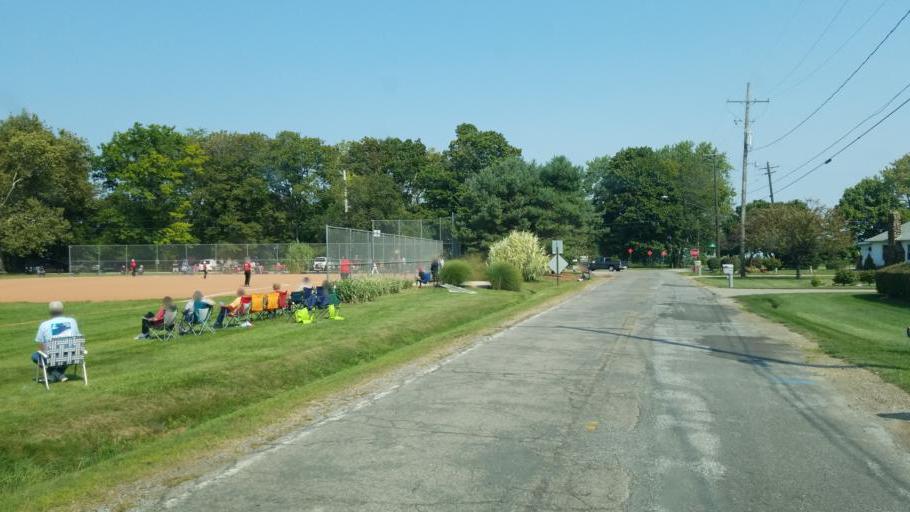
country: US
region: Ohio
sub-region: Lake County
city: Painesville
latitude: 41.7658
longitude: -81.2310
